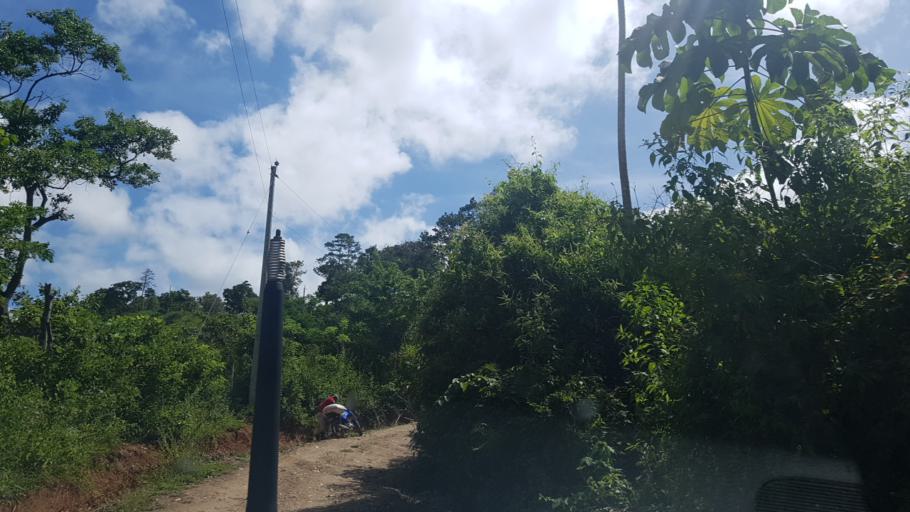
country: NI
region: Nueva Segovia
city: Ciudad Antigua
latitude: 13.6446
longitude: -86.2750
